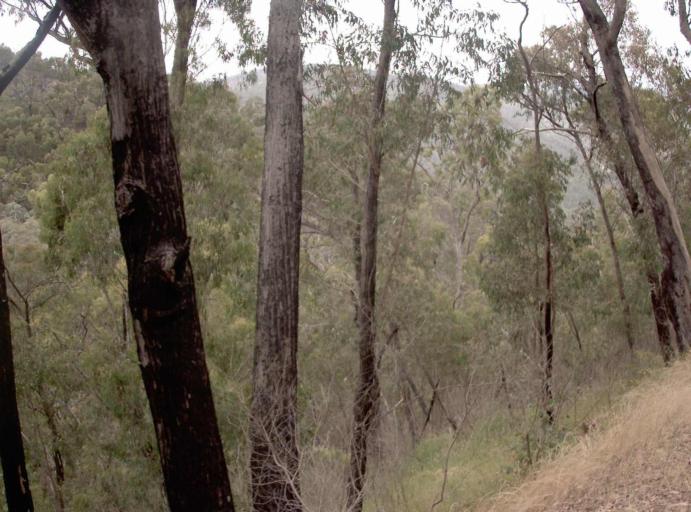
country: AU
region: Victoria
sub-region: Wellington
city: Heyfield
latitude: -37.7115
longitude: 146.6679
